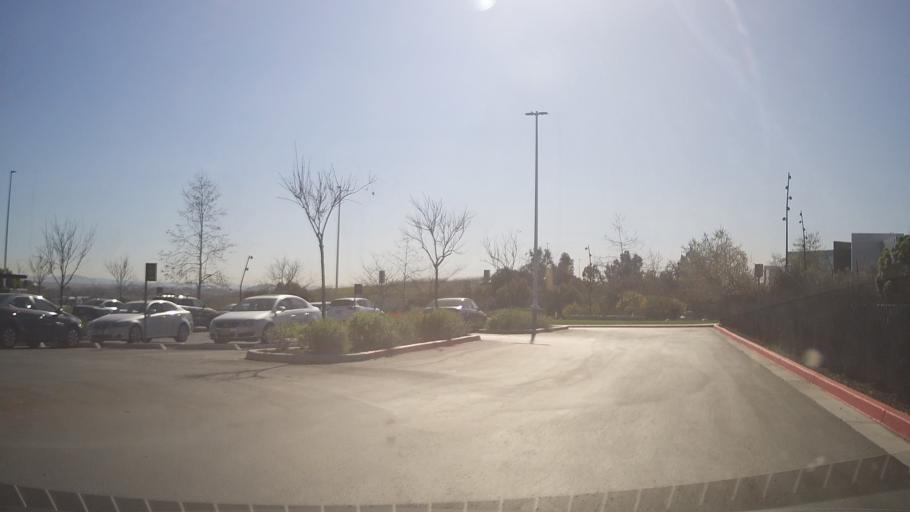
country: US
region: California
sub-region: San Diego County
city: La Jolla
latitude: 32.8948
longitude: -117.2242
